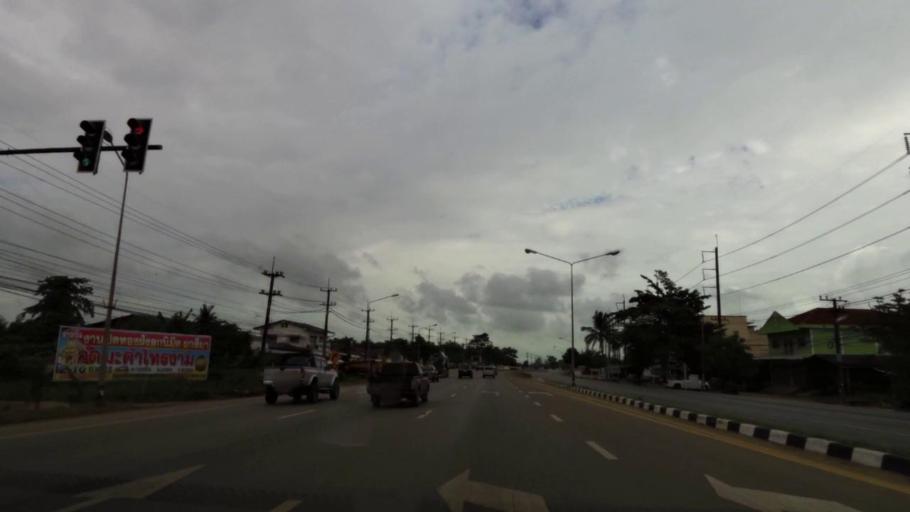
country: TH
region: Chanthaburi
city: Tha Mai
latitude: 12.7222
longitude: 101.9583
